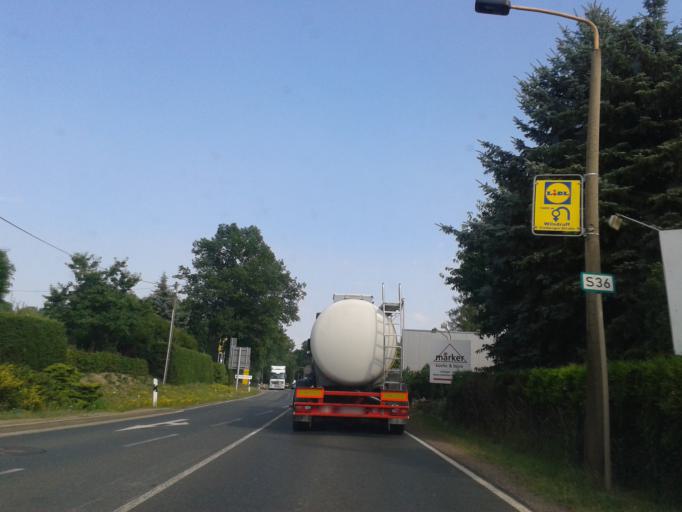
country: DE
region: Saxony
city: Wilsdruff
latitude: 51.0556
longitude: 13.5361
